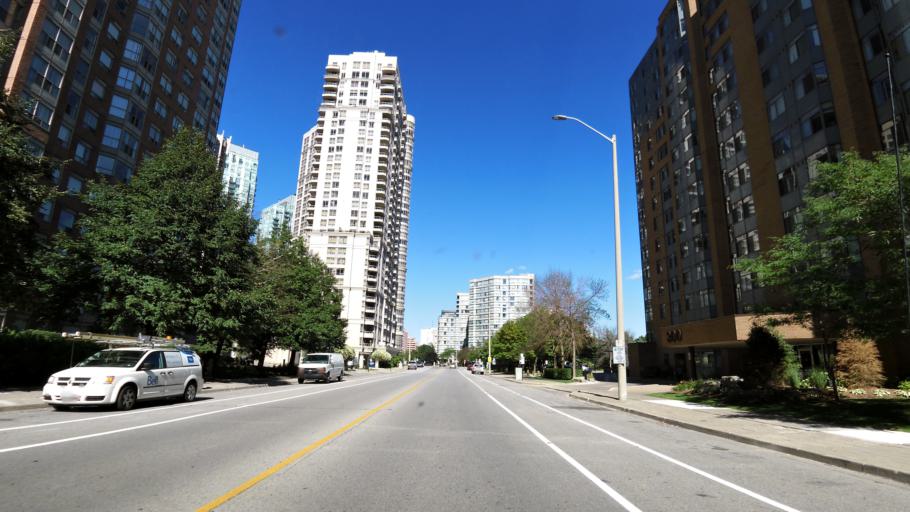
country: CA
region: Ontario
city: Mississauga
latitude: 43.5858
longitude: -79.6414
